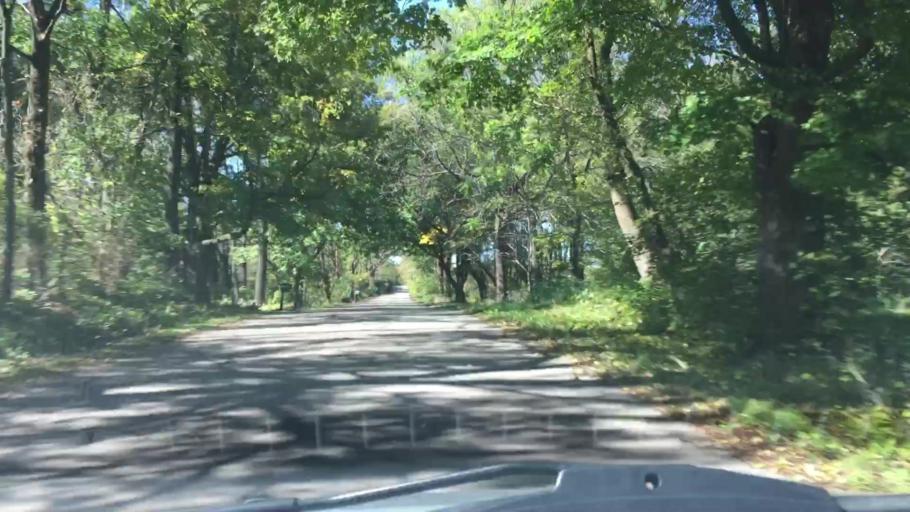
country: US
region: Wisconsin
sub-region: Waukesha County
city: North Prairie
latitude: 42.9303
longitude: -88.4411
